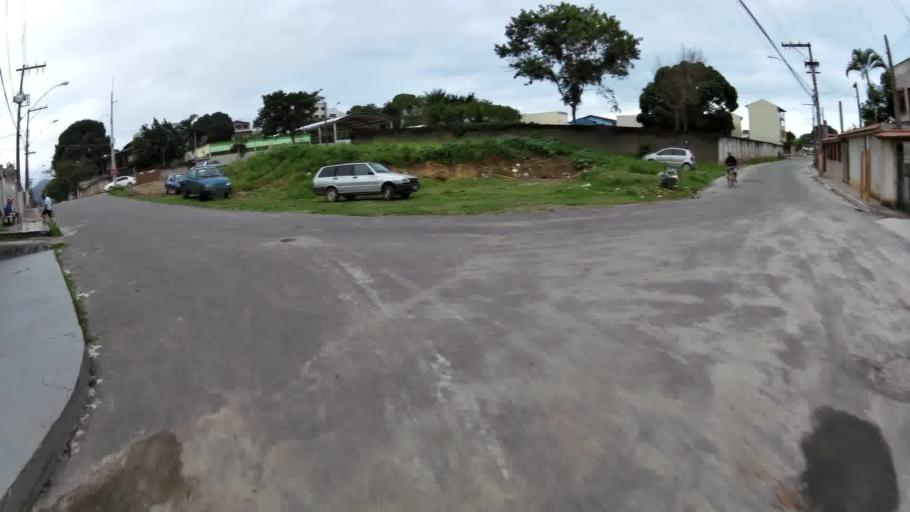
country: BR
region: Espirito Santo
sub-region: Guarapari
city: Guarapari
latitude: -20.6656
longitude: -40.5123
